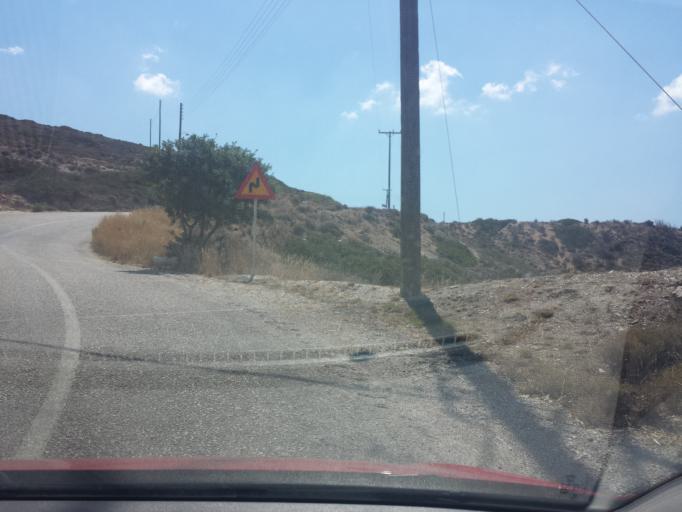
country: GR
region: South Aegean
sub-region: Nomos Kykladon
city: Adamas
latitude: 36.6862
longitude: 24.5016
